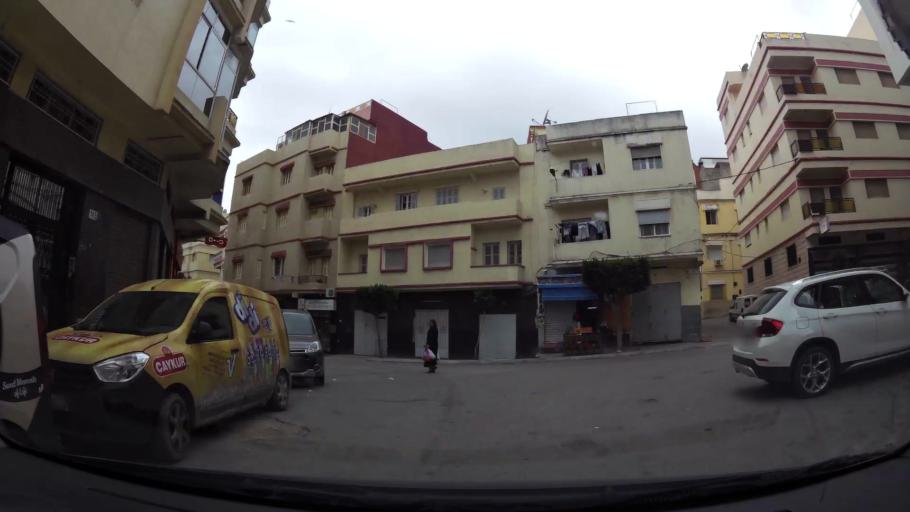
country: MA
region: Tanger-Tetouan
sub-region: Tanger-Assilah
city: Tangier
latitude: 35.7721
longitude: -5.8166
